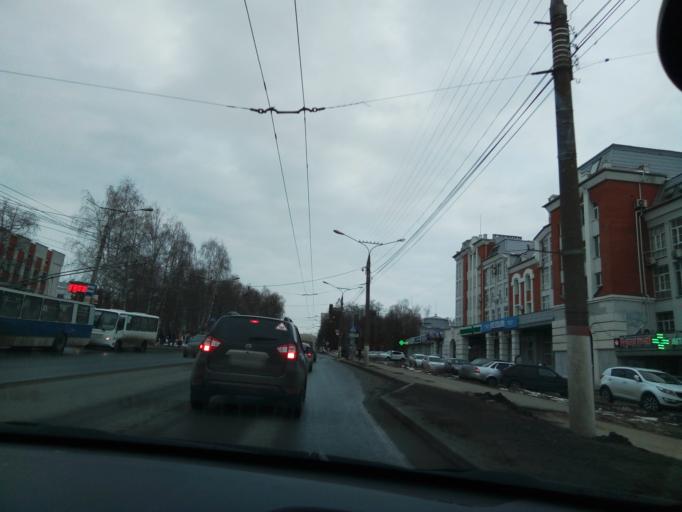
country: RU
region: Chuvashia
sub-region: Cheboksarskiy Rayon
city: Cheboksary
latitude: 56.1463
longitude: 47.2288
